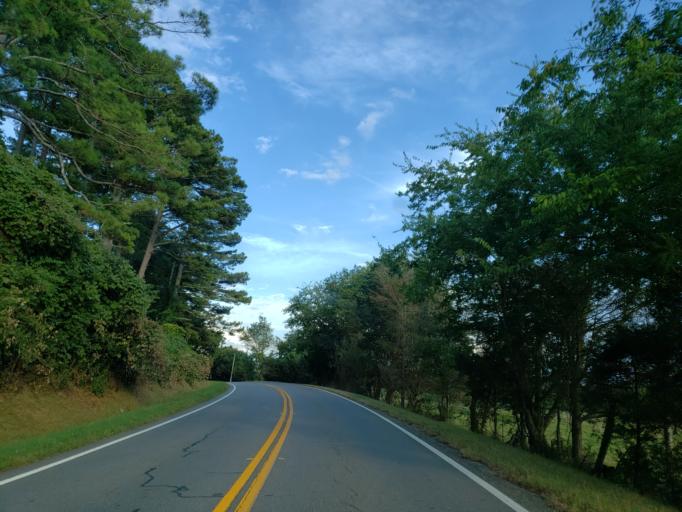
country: US
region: Georgia
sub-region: Bartow County
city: Euharlee
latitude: 34.2414
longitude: -84.8870
